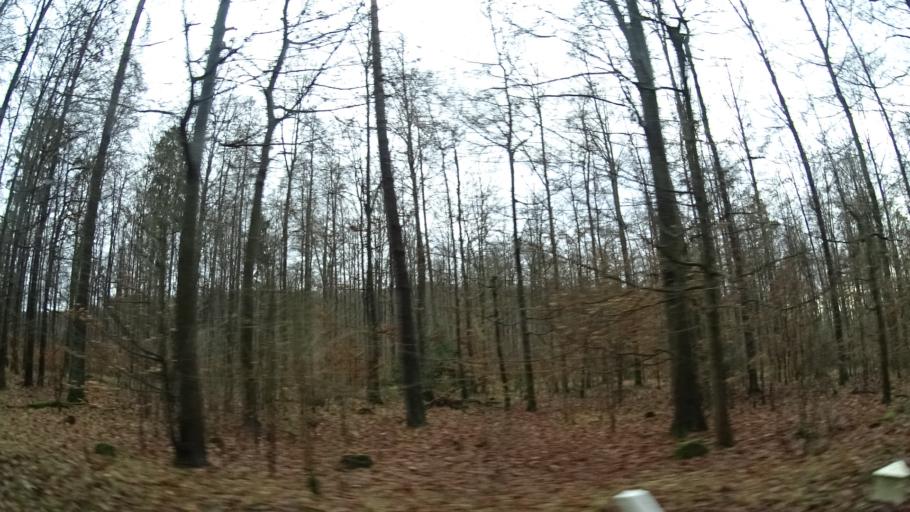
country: DE
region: Bavaria
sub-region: Regierungsbezirk Unterfranken
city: Willmars
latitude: 50.5379
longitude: 10.2359
